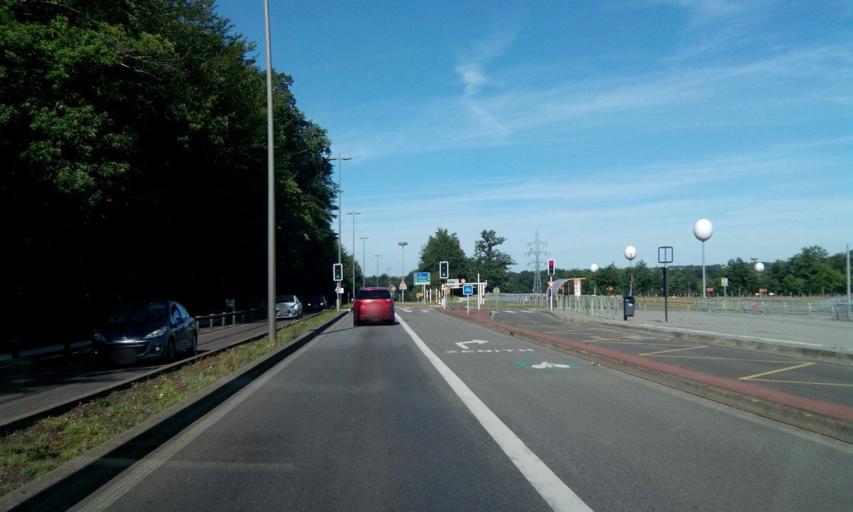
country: FR
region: Limousin
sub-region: Departement de la Haute-Vienne
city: Limoges
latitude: 45.8613
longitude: 1.2797
